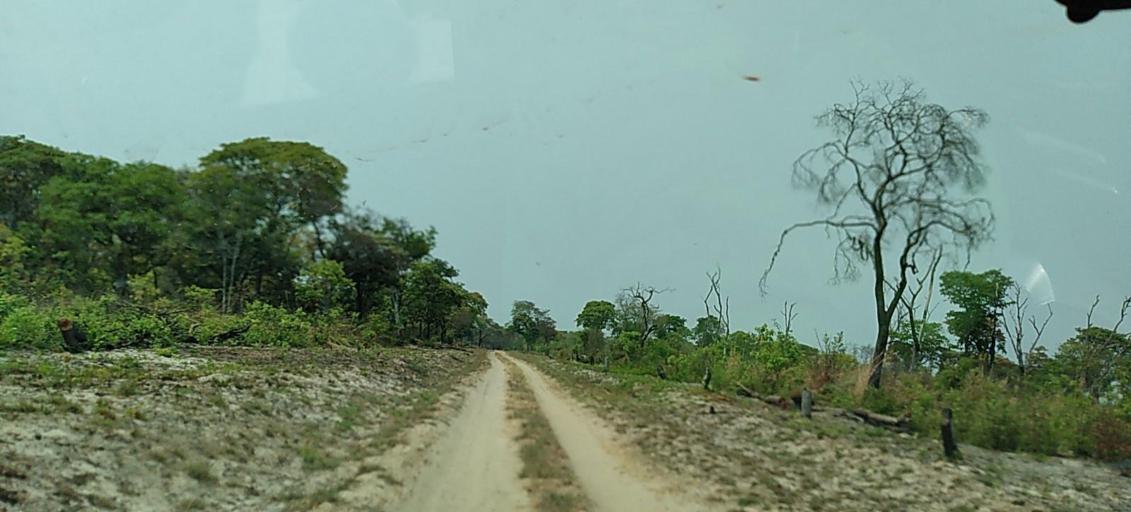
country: ZM
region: Western
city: Lukulu
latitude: -13.9611
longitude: 23.2251
